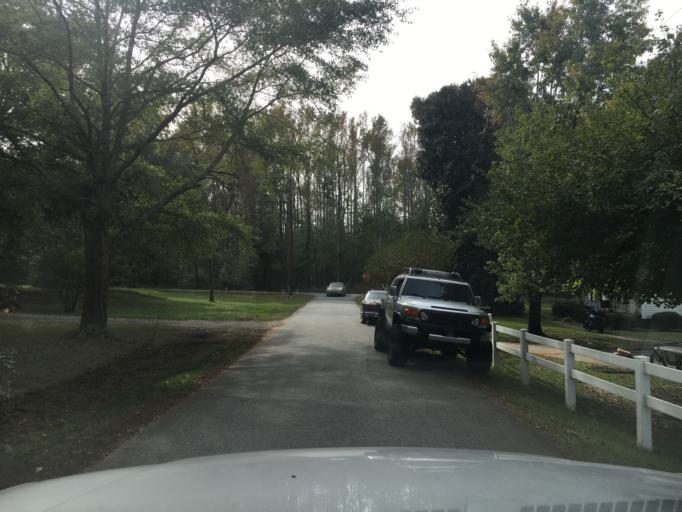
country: US
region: South Carolina
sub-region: Spartanburg County
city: Duncan
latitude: 34.8660
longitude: -82.1141
